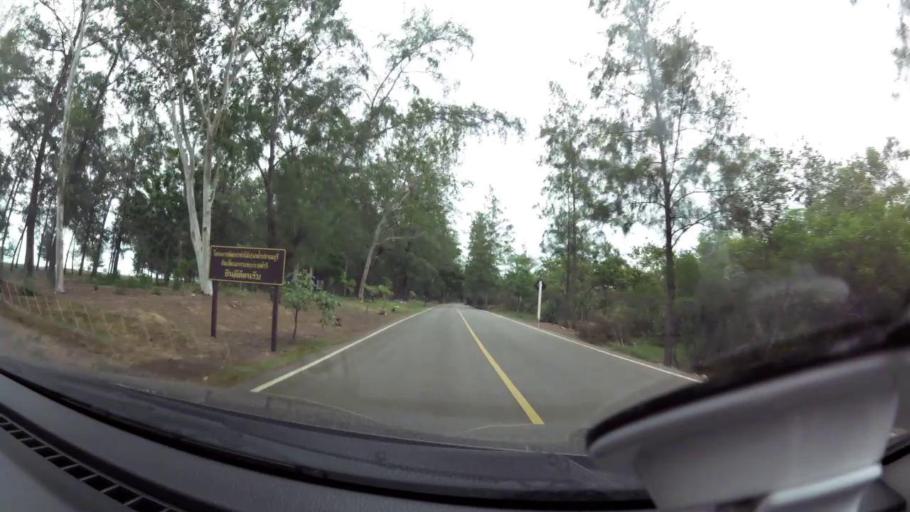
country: TH
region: Prachuap Khiri Khan
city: Pran Buri
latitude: 12.4182
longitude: 99.9840
